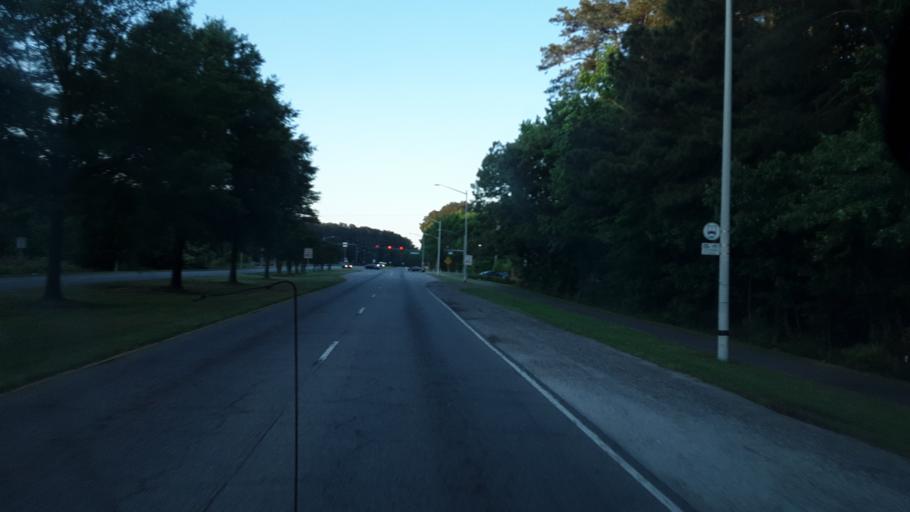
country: US
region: Virginia
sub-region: City of Virginia Beach
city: Virginia Beach
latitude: 36.7956
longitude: -75.9949
